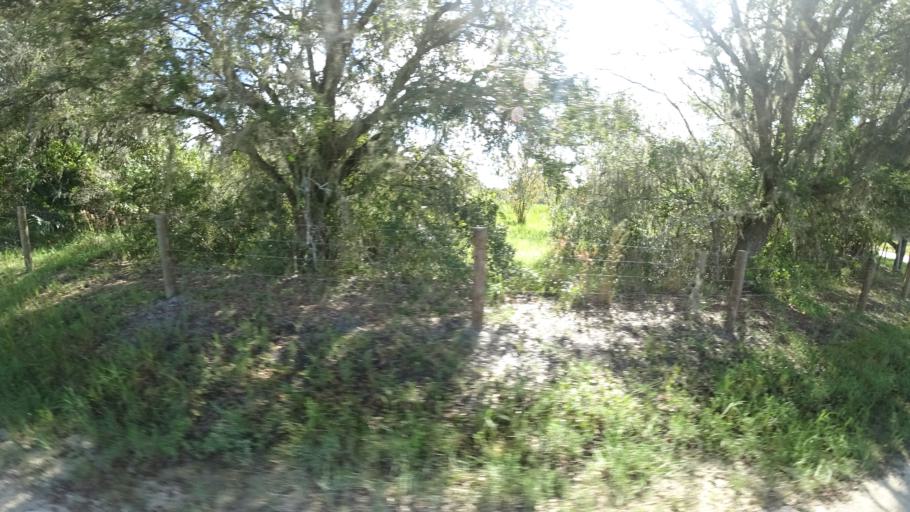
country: US
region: Florida
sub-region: Sarasota County
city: Lake Sarasota
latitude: 27.3212
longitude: -82.2200
